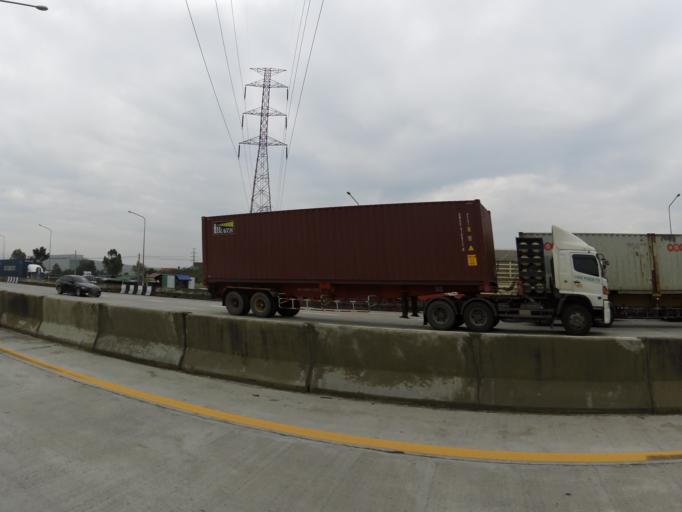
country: TH
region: Chon Buri
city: Ban Talat Bueng
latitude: 13.1164
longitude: 100.9772
